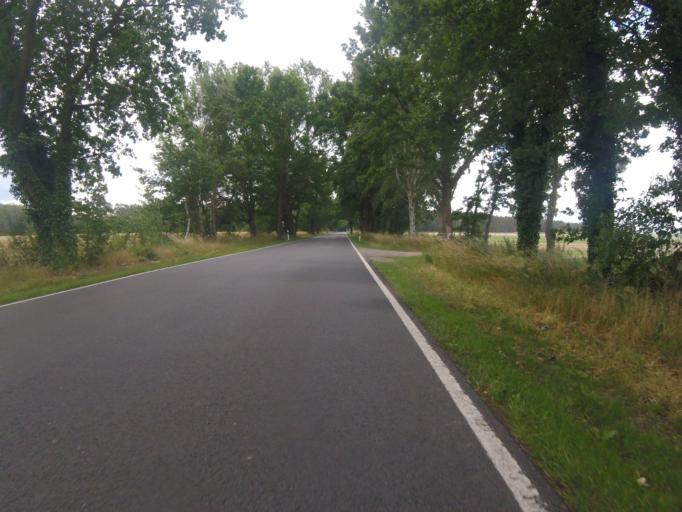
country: DE
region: Brandenburg
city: Bestensee
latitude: 52.2667
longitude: 13.7337
